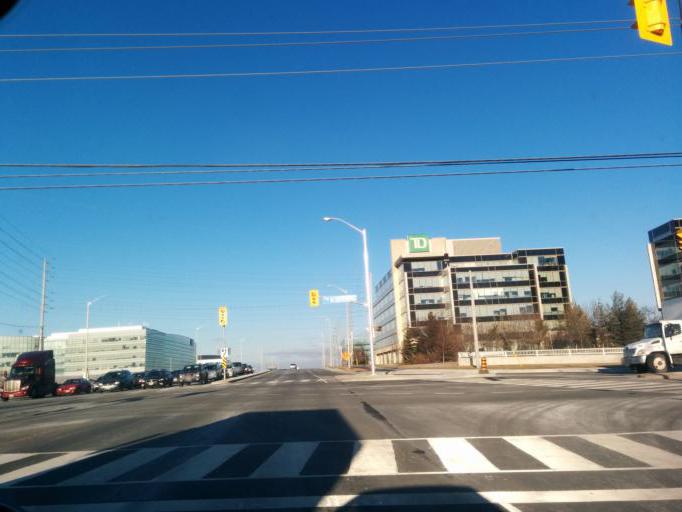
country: CA
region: Ontario
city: Etobicoke
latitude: 43.6411
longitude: -79.6147
